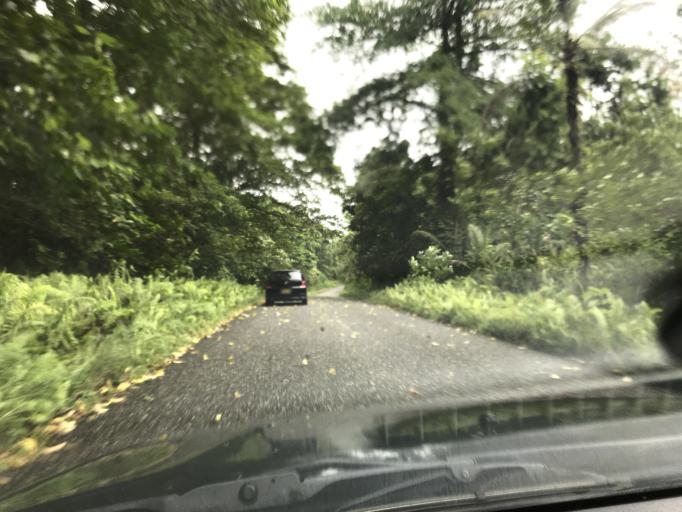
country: SB
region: Western Province
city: Gizo
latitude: -8.2361
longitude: 157.2186
